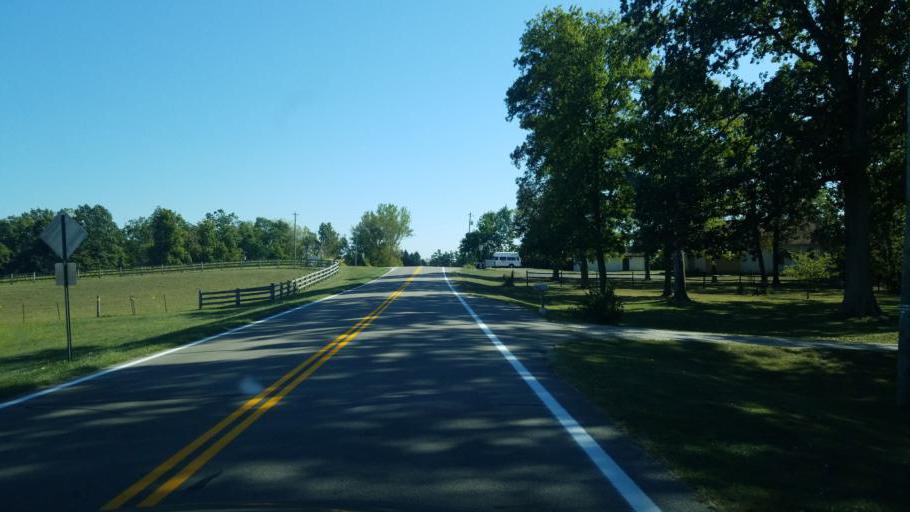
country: US
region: Ohio
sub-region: Champaign County
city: Mechanicsburg
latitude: 40.1083
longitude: -83.5807
